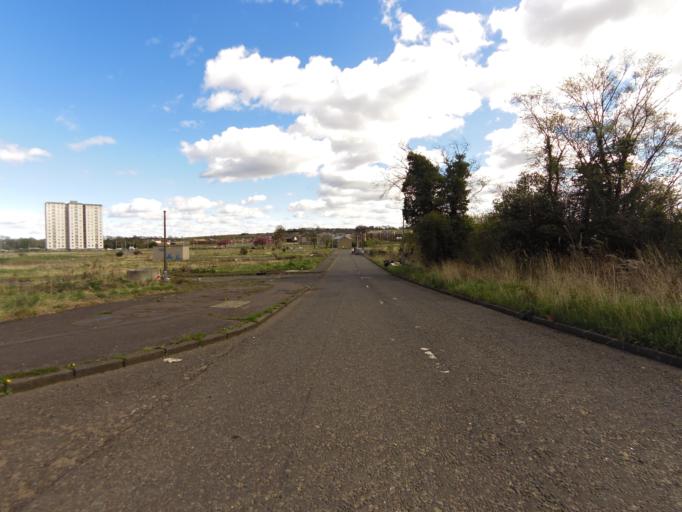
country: GB
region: Scotland
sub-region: West Lothian
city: Seafield
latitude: 55.9276
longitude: -3.1290
